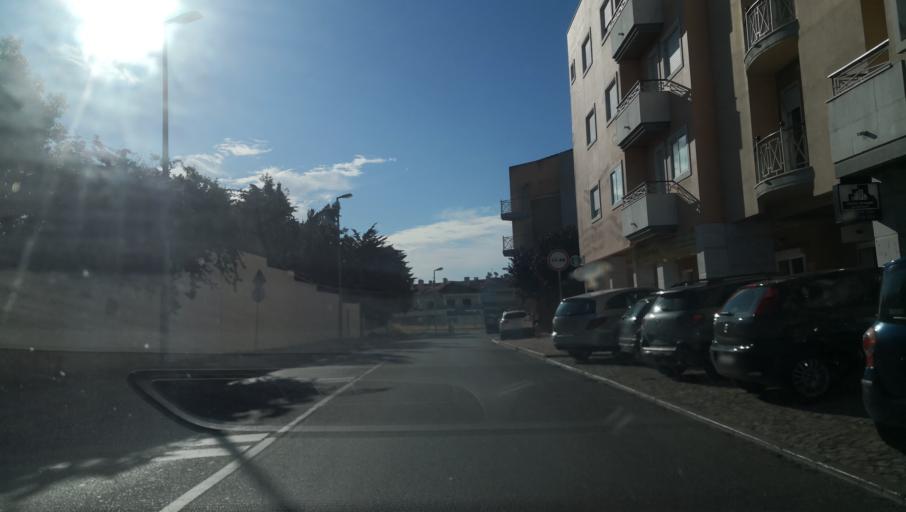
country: PT
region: Lisbon
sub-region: Oeiras
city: Carcavelos
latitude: 38.6848
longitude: -9.3269
